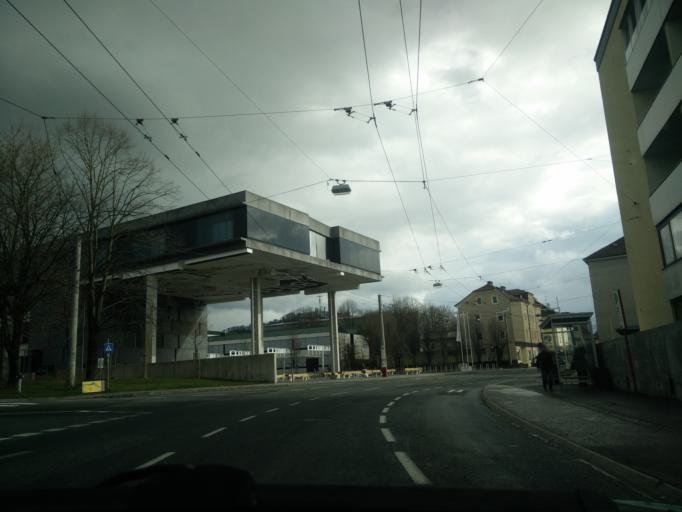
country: AT
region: Salzburg
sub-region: Politischer Bezirk Salzburg-Umgebung
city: Bergheim
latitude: 47.8224
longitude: 13.0443
